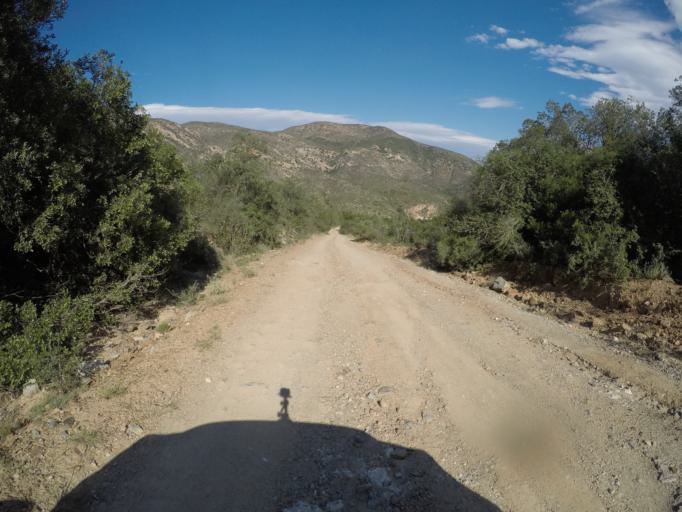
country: ZA
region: Eastern Cape
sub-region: Cacadu District Municipality
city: Kareedouw
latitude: -33.6447
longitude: 24.4573
